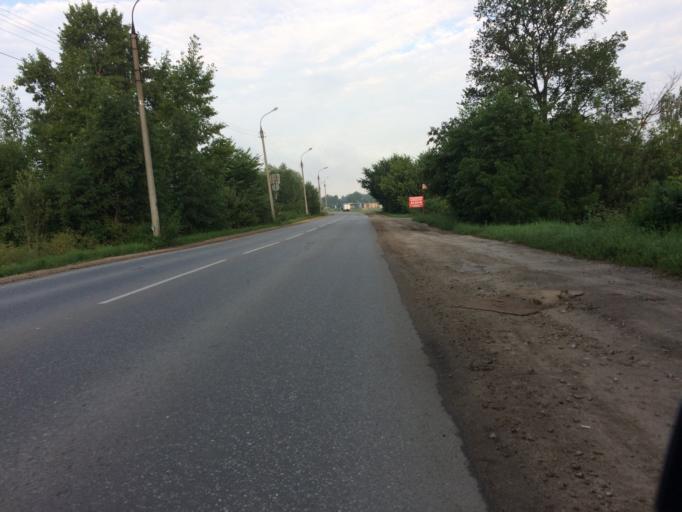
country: RU
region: Mariy-El
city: Yoshkar-Ola
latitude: 56.6465
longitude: 47.9467
